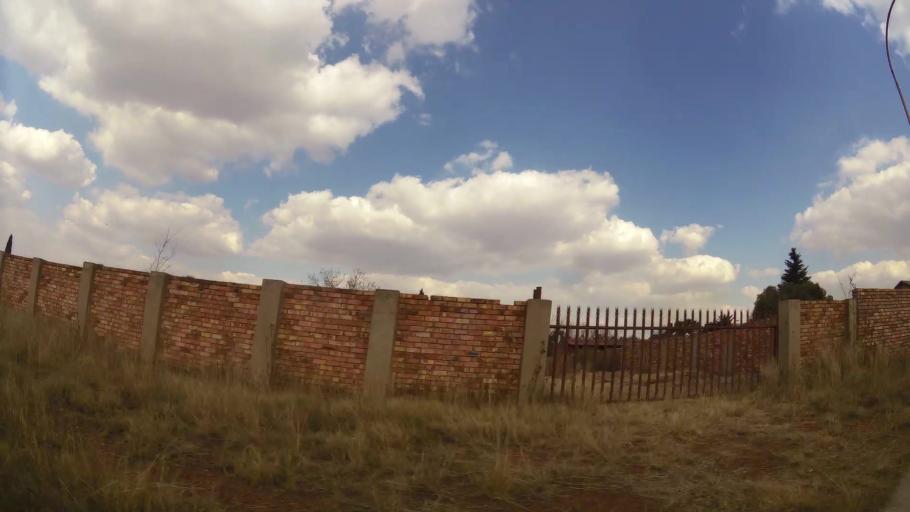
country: ZA
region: Mpumalanga
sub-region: Nkangala District Municipality
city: Delmas
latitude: -26.1363
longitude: 28.6742
